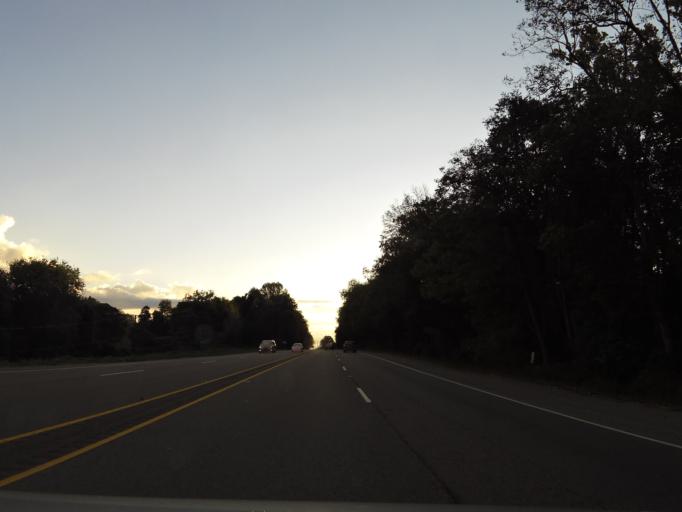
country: US
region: Tennessee
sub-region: Knox County
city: Mascot
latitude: 36.0556
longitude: -83.6985
